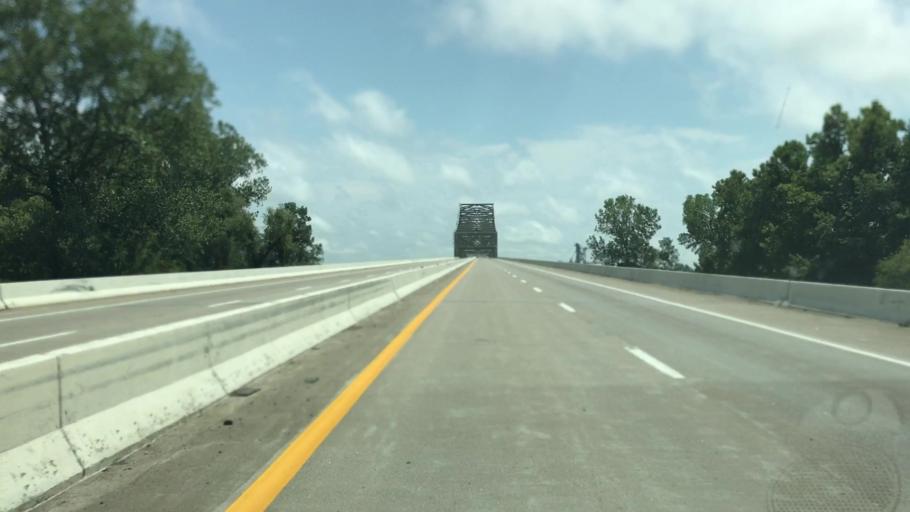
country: US
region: Missouri
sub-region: Pemiscot County
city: Caruthersville
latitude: 36.1197
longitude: -89.6158
